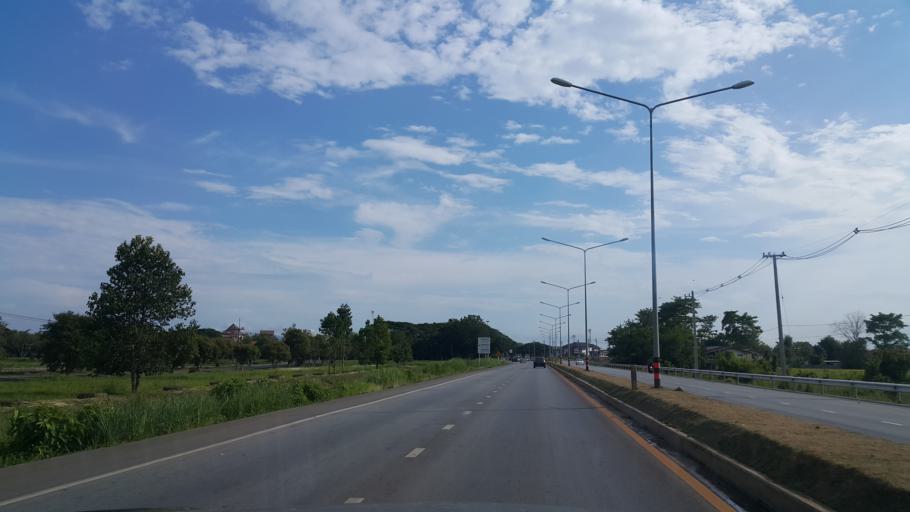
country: TH
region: Chiang Rai
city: Chiang Rai
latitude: 19.9359
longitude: 99.8659
